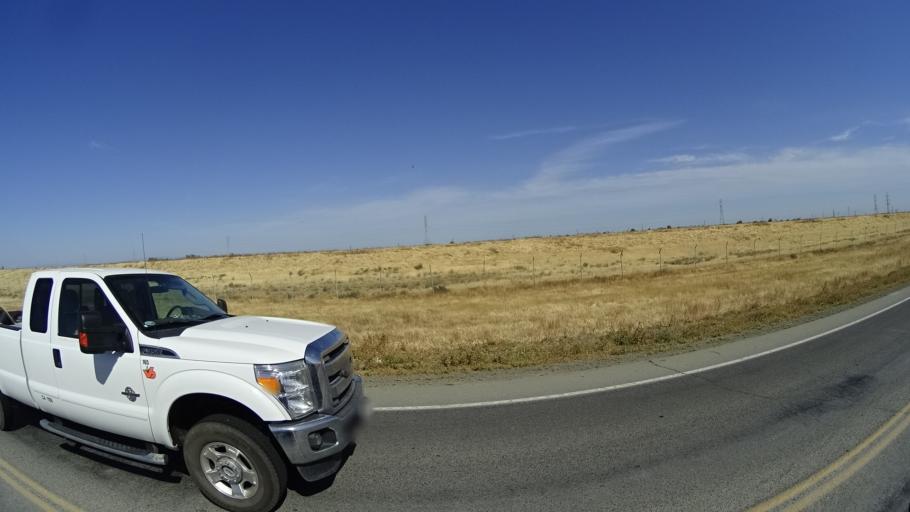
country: US
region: California
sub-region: Kings County
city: Lemoore Station
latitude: 36.2468
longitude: -119.8719
